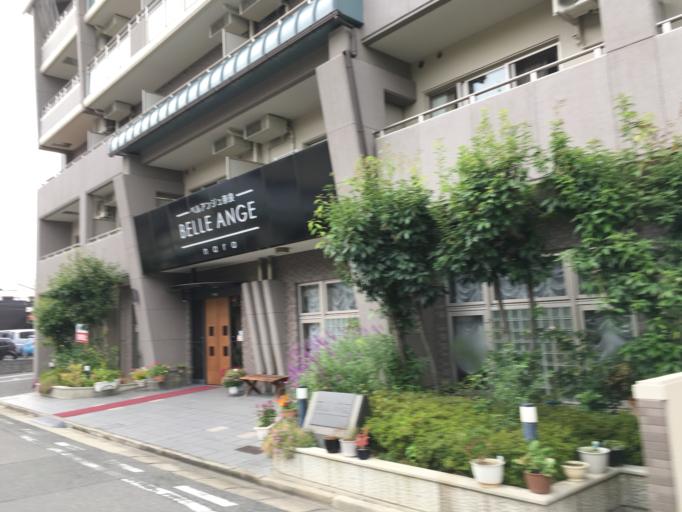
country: JP
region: Nara
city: Nara-shi
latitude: 34.6865
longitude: 135.8104
